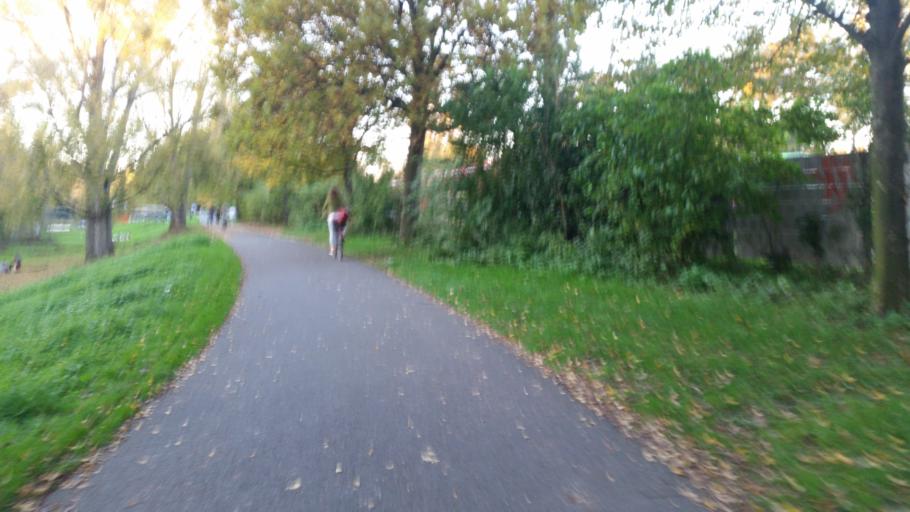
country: DE
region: Lower Saxony
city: Hannover
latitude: 52.3752
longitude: 9.7152
